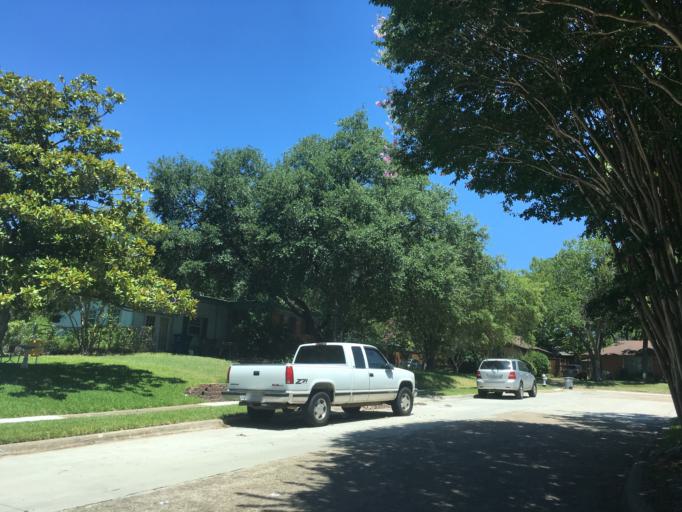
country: US
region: Texas
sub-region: Dallas County
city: Highland Park
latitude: 32.8461
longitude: -96.7056
